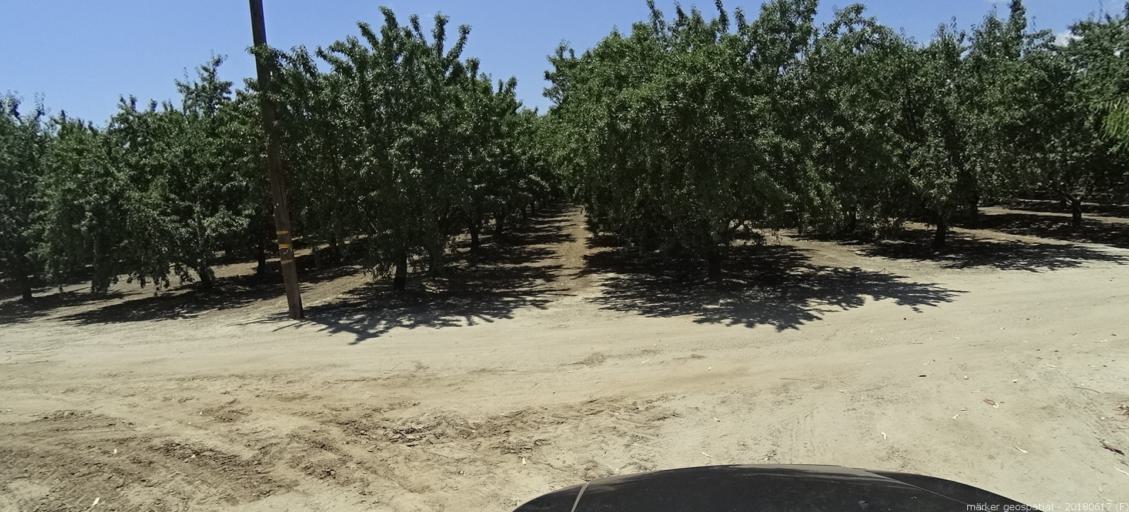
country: US
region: California
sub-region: Madera County
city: Parkwood
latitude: 36.8356
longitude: -120.1757
